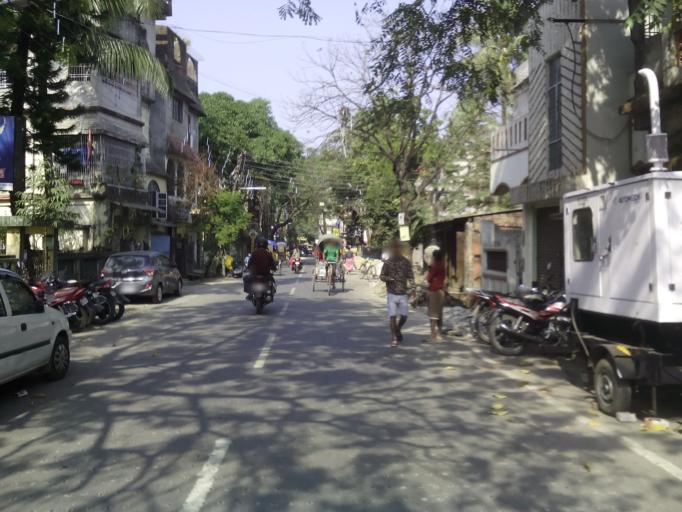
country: IN
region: West Bengal
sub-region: Darjiling
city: Shiliguri
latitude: 26.7084
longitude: 88.4341
